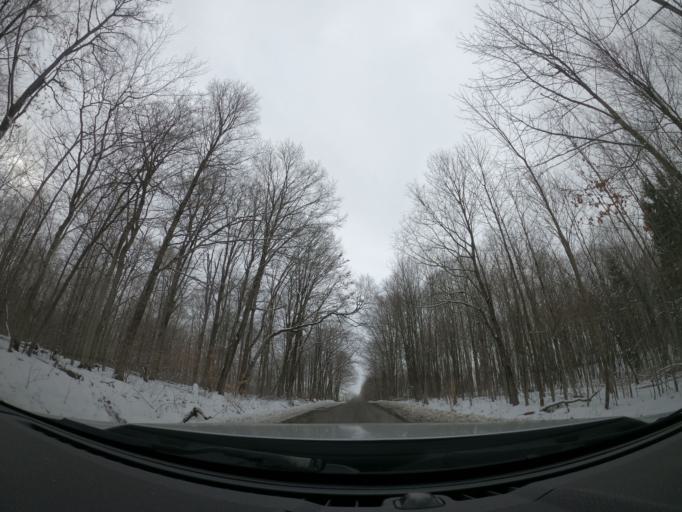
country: US
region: New York
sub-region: Cayuga County
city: Moravia
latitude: 42.7339
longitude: -76.3018
